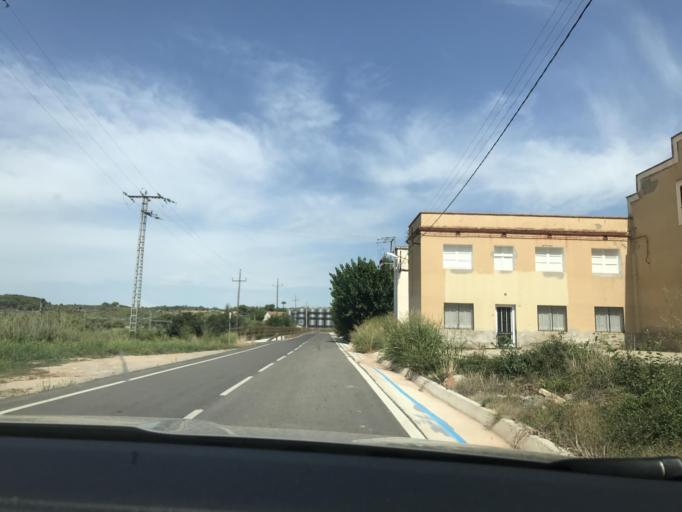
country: ES
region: Catalonia
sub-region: Provincia de Tarragona
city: Salomo
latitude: 41.2238
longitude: 1.3773
